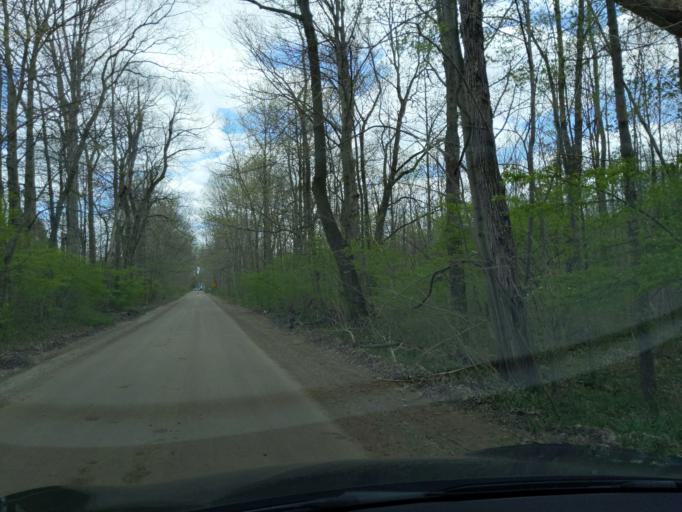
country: US
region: Michigan
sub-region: Eaton County
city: Dimondale
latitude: 42.6272
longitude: -84.6076
